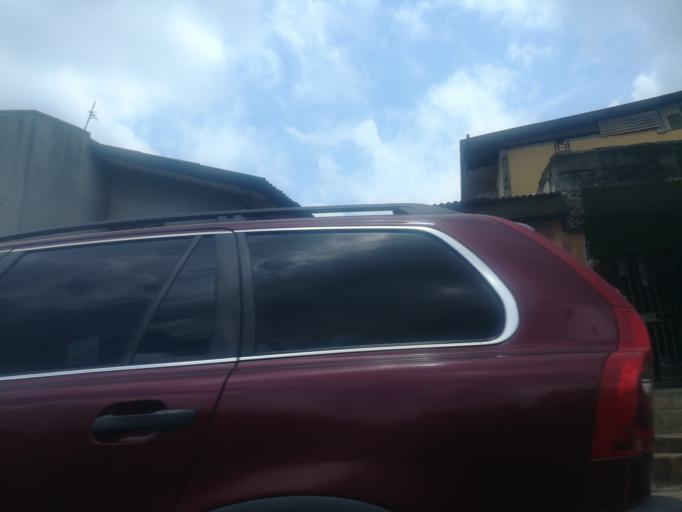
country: NG
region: Lagos
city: Somolu
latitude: 6.5584
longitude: 3.3931
